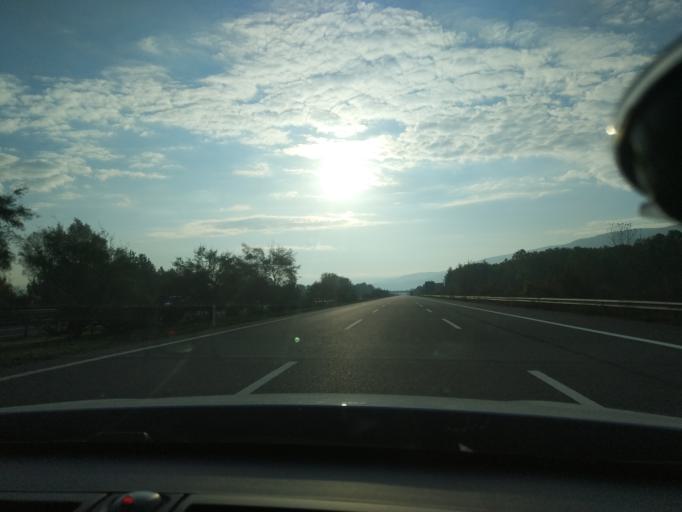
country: TR
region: Duzce
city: Duzce
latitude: 40.8020
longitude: 31.1770
